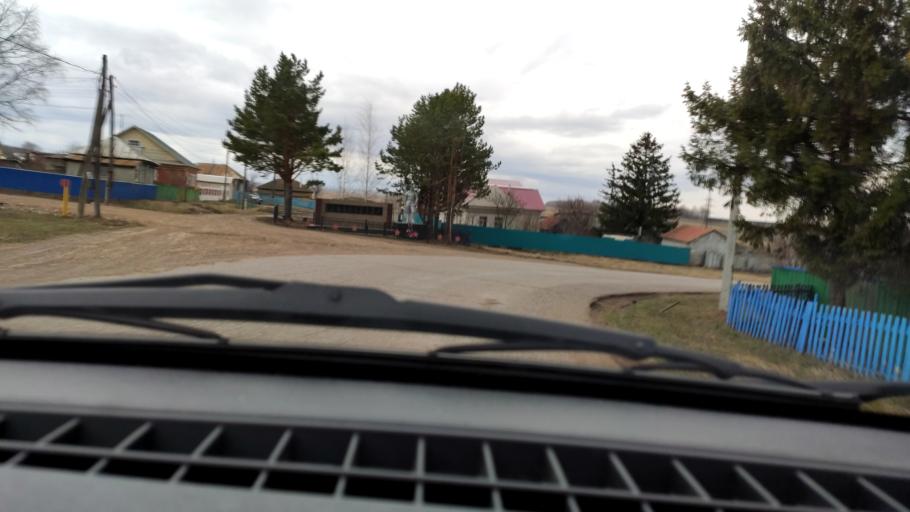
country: RU
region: Bashkortostan
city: Semiletka
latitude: 55.2818
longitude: 54.6569
